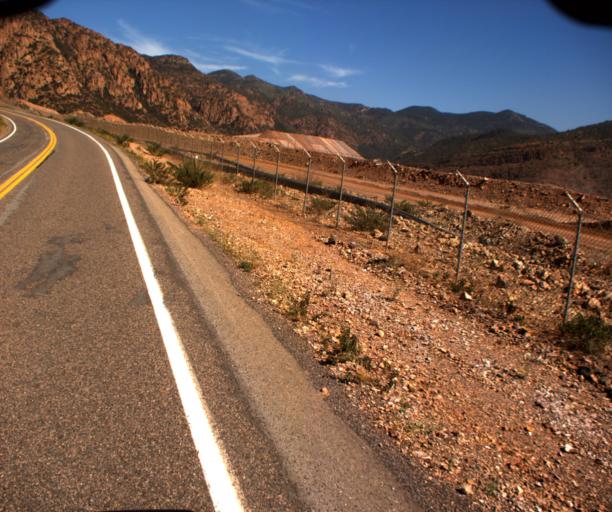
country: US
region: Arizona
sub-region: Greenlee County
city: Morenci
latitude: 33.1266
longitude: -109.3693
